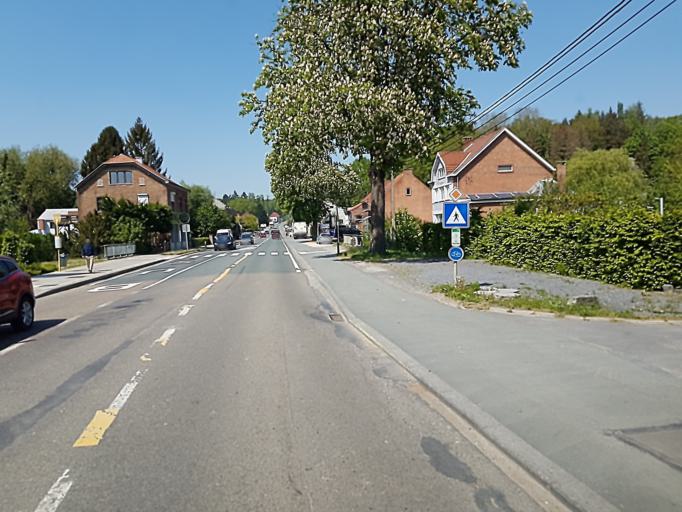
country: BE
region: Wallonia
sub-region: Province du Brabant Wallon
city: Grez-Doiceau
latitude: 50.7815
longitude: 4.7157
